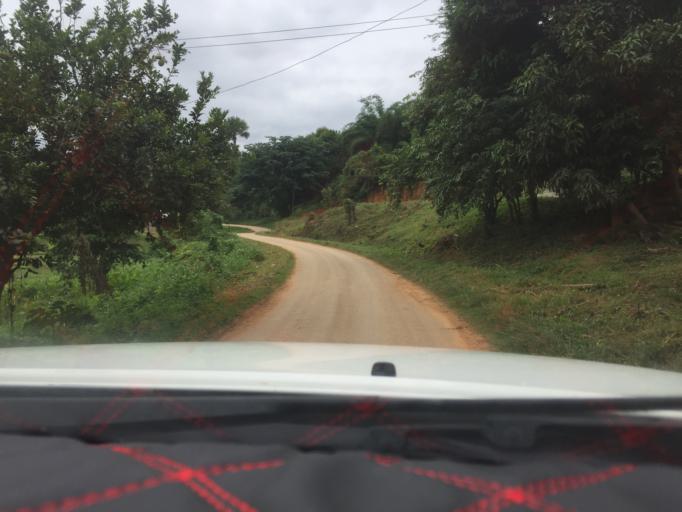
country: TH
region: Phayao
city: Phu Sang
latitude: 19.7700
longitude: 100.5457
